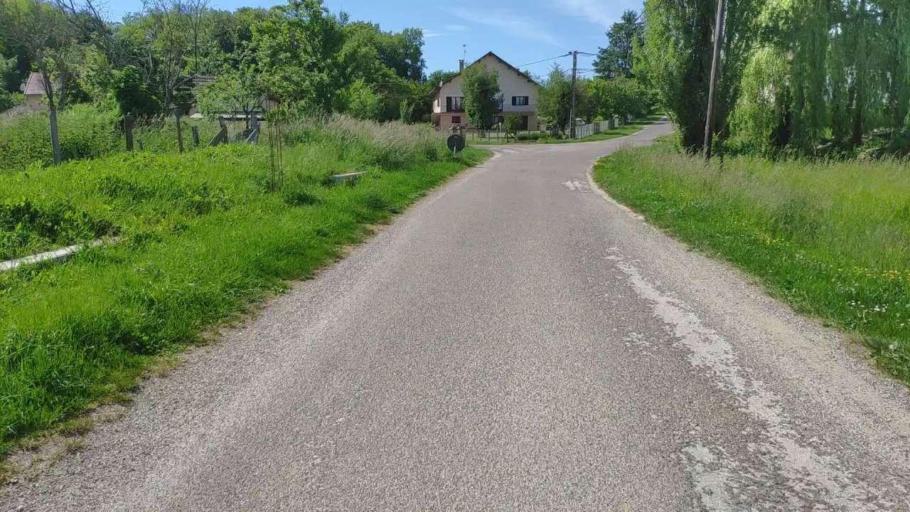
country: FR
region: Franche-Comte
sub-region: Departement du Jura
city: Bletterans
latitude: 46.7686
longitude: 5.4742
